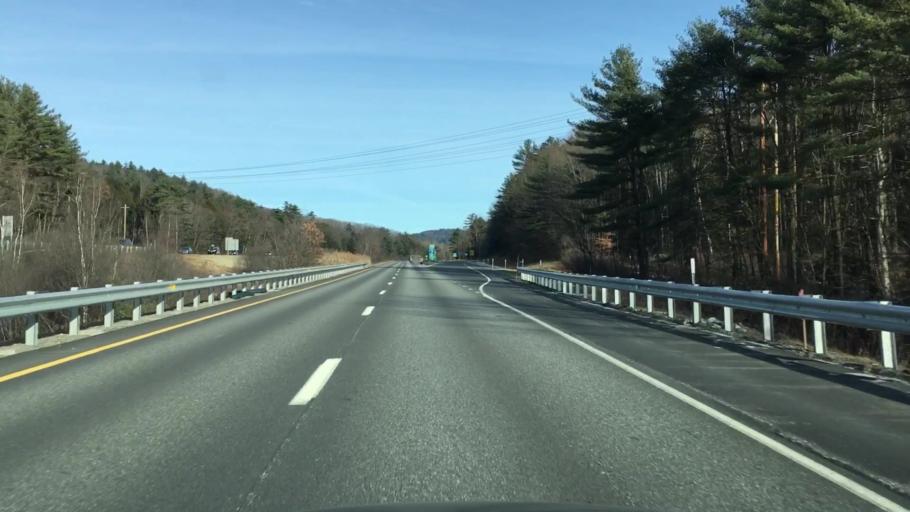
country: US
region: New Hampshire
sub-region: Grafton County
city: Lebanon
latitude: 43.6463
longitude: -72.2665
